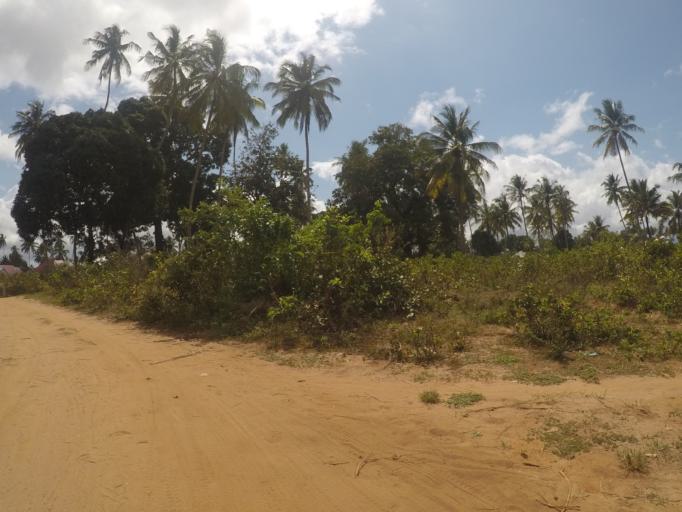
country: TZ
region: Zanzibar Urban/West
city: Zanzibar
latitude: -6.2021
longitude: 39.2335
